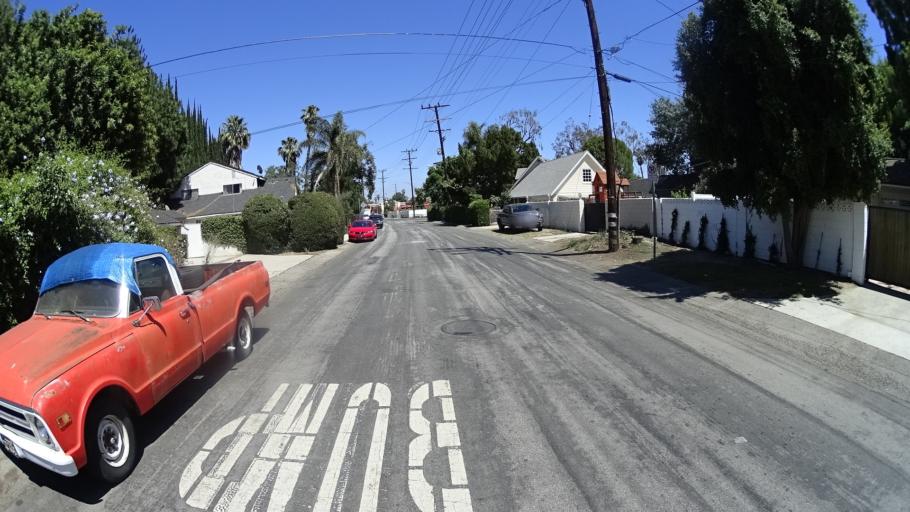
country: US
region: California
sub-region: Los Angeles County
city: Van Nuys
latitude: 34.1888
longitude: -118.4685
